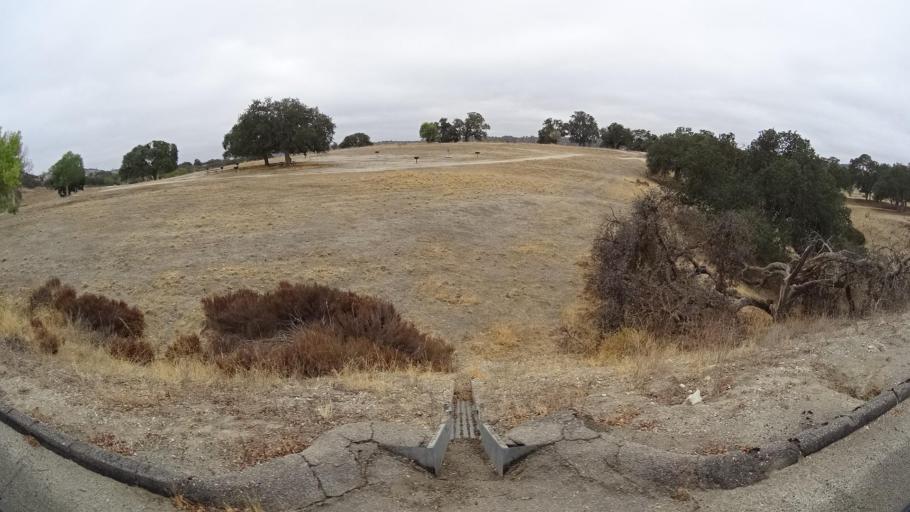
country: US
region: California
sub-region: San Luis Obispo County
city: Lake Nacimiento
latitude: 35.8667
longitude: -120.9749
